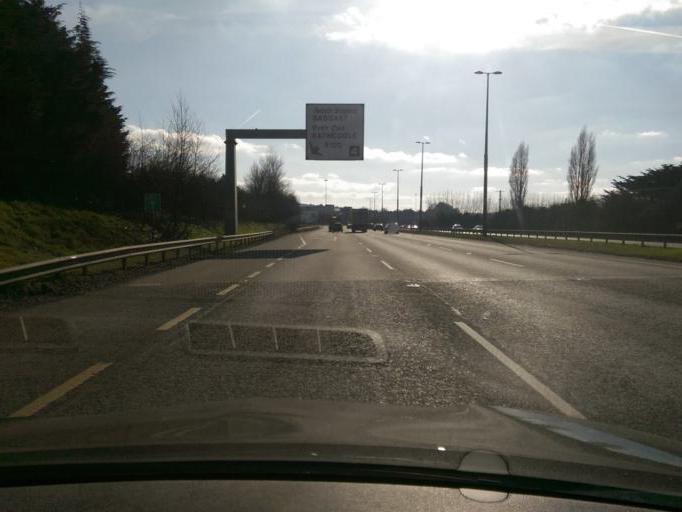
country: IE
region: Leinster
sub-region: South Dublin
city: Saggart
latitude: 53.2876
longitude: -6.4511
